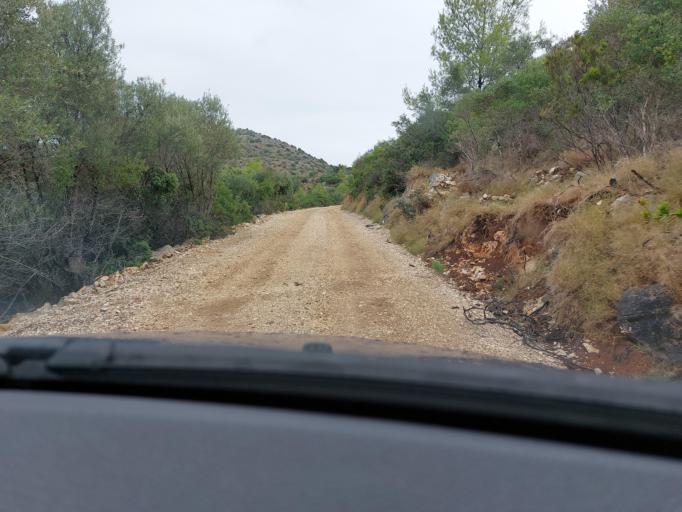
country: HR
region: Dubrovacko-Neretvanska
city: Smokvica
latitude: 42.7384
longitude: 16.9080
